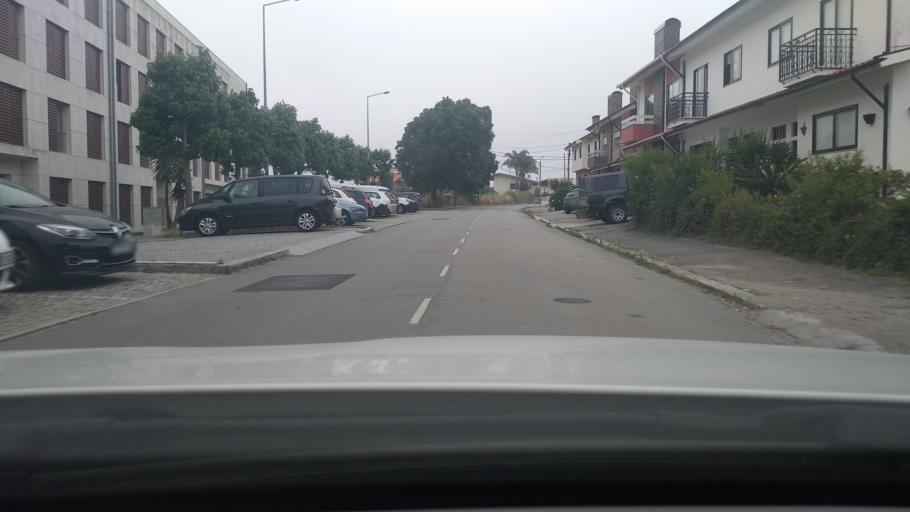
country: PT
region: Aveiro
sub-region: Espinho
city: Silvalde
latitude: 41.0027
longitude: -8.6270
